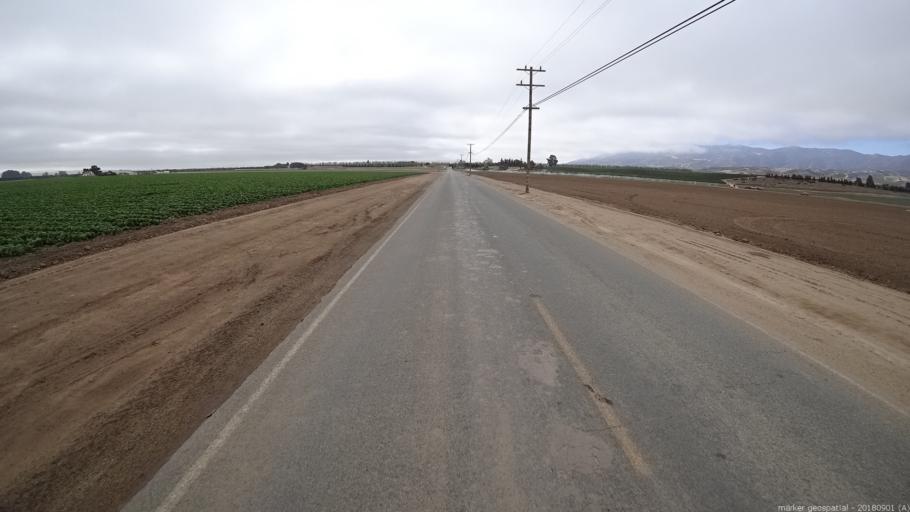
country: US
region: California
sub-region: Monterey County
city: Soledad
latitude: 36.3797
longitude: -121.3285
